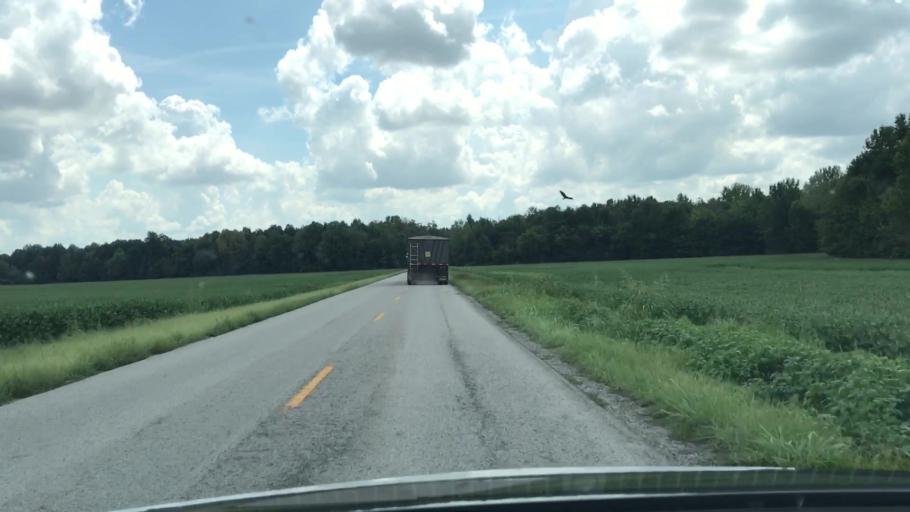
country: US
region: Kentucky
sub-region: Todd County
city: Guthrie
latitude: 36.6850
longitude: -87.0261
